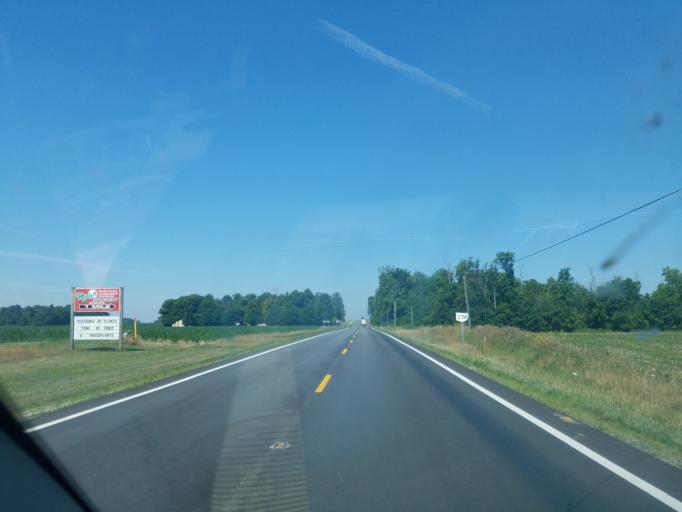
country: US
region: Ohio
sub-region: Shelby County
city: Jackson Center
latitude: 40.4394
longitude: -84.0973
